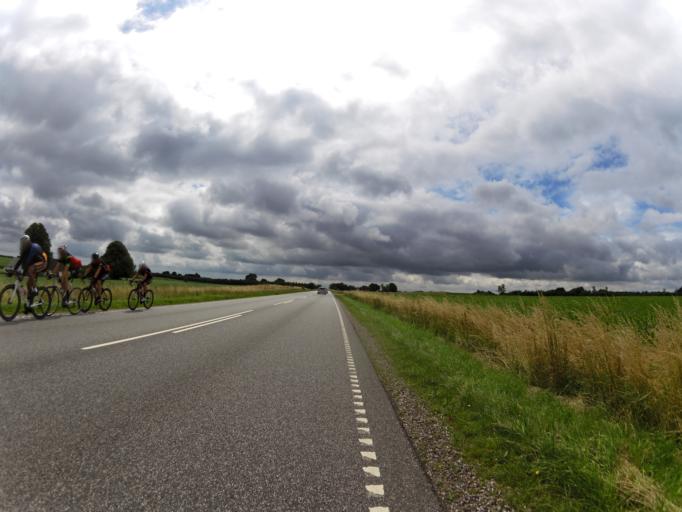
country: DK
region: North Denmark
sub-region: Mariagerfjord Kommune
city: Hadsund
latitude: 56.6715
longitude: 10.1474
